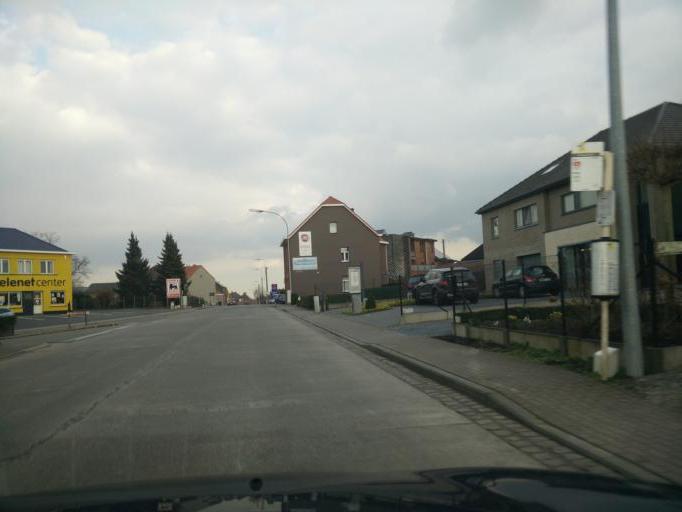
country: BE
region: Flanders
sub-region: Provincie Oost-Vlaanderen
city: Zottegem
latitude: 50.8640
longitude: 3.8261
